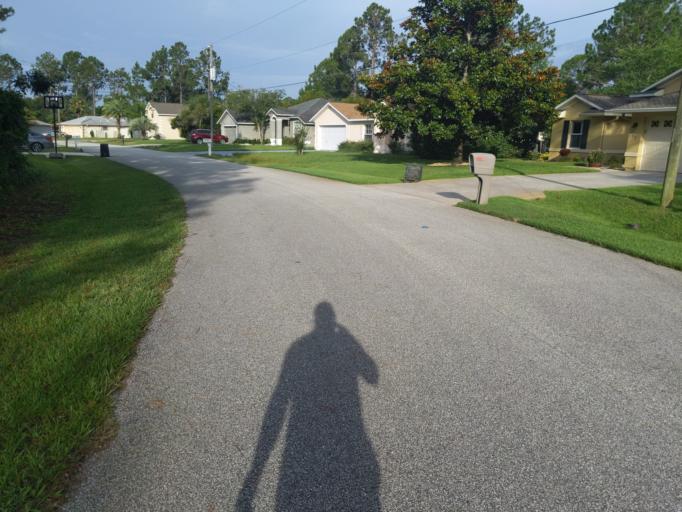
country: US
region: Florida
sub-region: Flagler County
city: Bunnell
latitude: 29.5221
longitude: -81.2384
